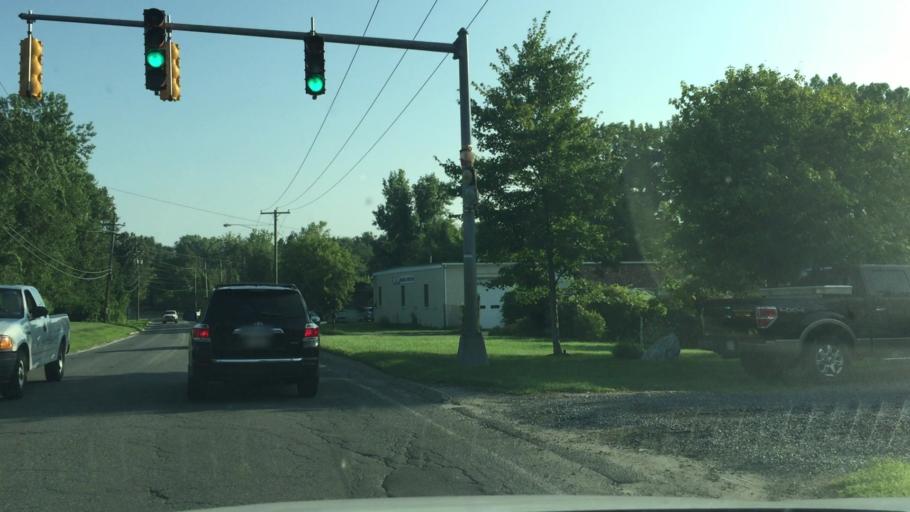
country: US
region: Massachusetts
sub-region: Berkshire County
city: Dalton
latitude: 42.4596
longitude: -73.1891
